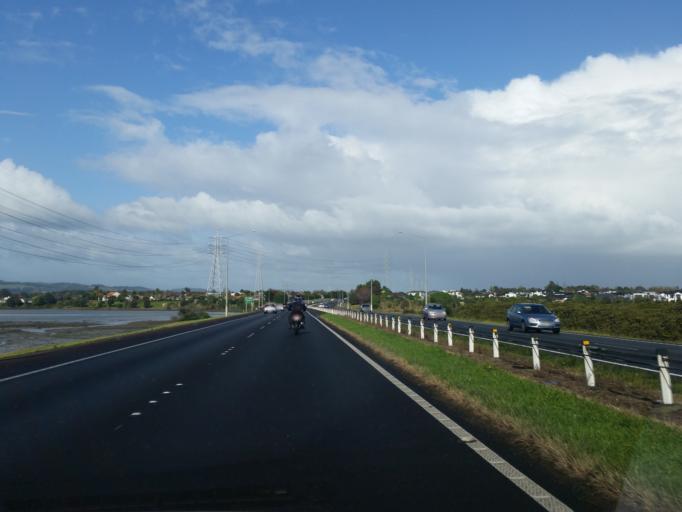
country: NZ
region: Auckland
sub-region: Auckland
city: Takanini
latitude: -37.0569
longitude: 174.9214
